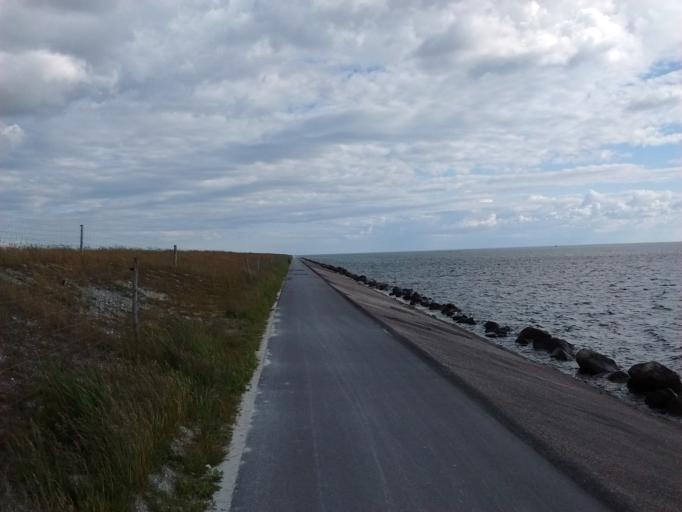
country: DK
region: Capital Region
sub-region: Hvidovre Kommune
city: Hvidovre
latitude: 55.6038
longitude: 12.5099
